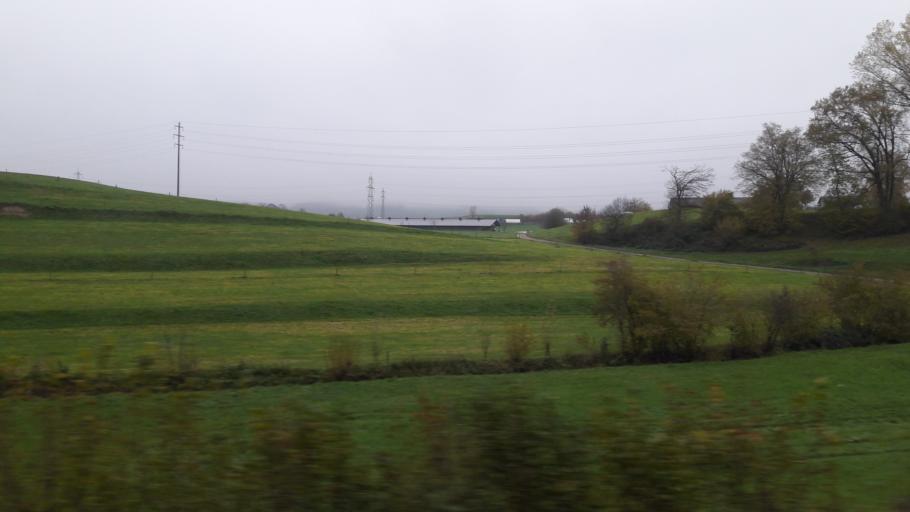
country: CH
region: Bern
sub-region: Oberaargau
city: Oberbipp
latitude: 47.2468
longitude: 7.6741
